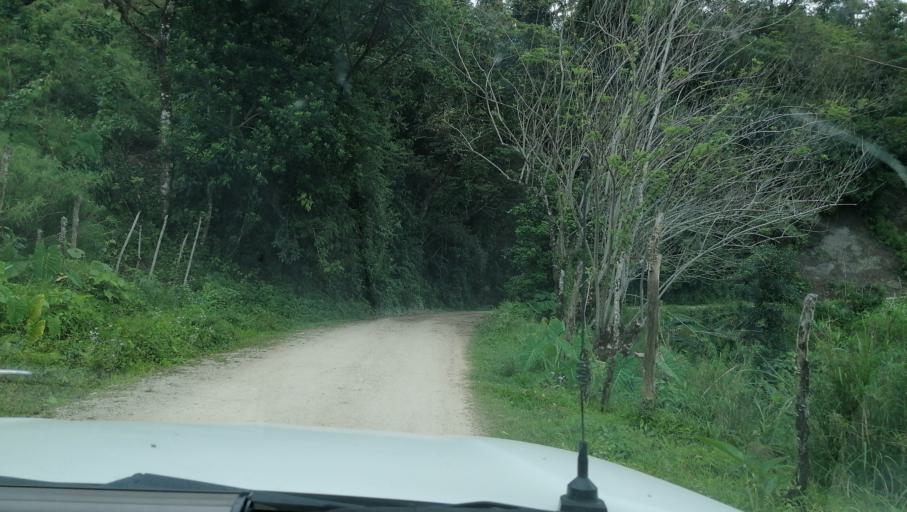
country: MX
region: Chiapas
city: Ocotepec
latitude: 17.2769
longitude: -93.2262
